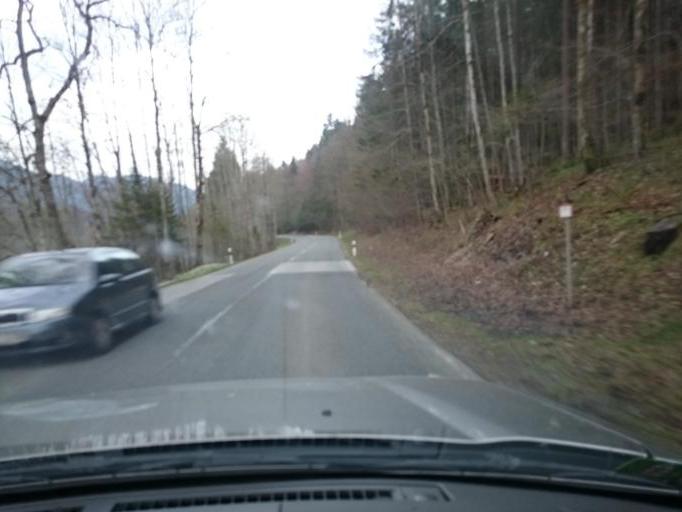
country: DE
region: Bavaria
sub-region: Upper Bavaria
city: Oberammergau
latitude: 47.5696
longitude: 11.0697
